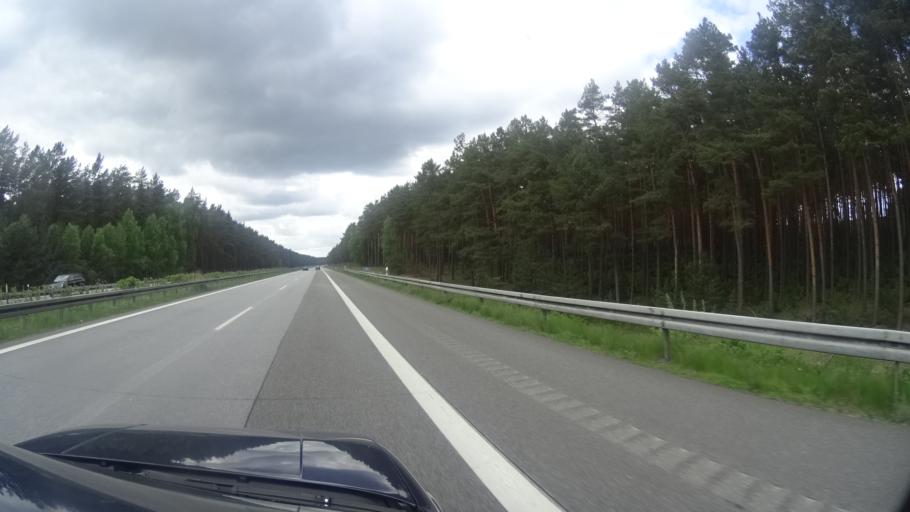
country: DE
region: Mecklenburg-Vorpommern
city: Plau am See
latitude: 53.5452
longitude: 12.3339
